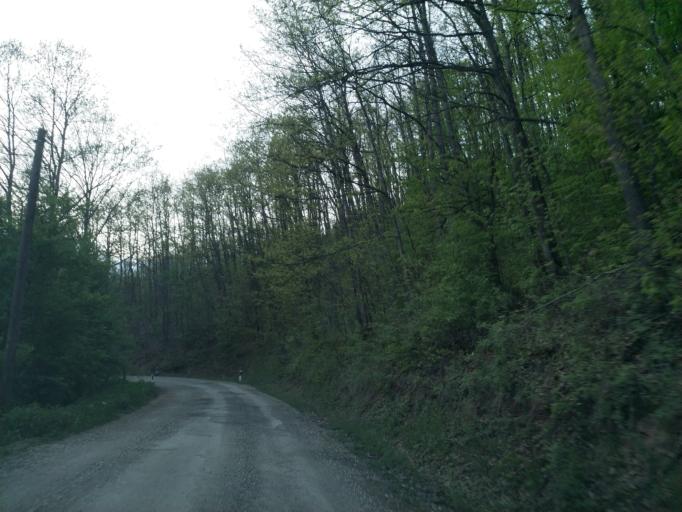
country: RS
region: Central Serbia
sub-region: Pomoravski Okrug
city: Despotovac
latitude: 43.9556
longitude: 21.5706
